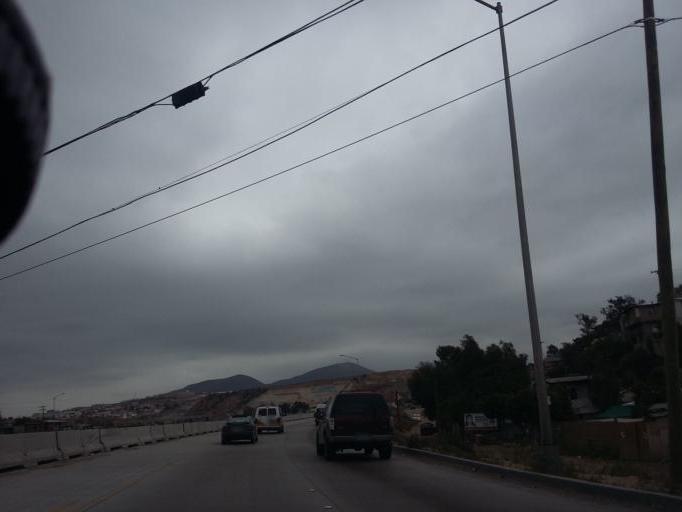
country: MX
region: Baja California
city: Tijuana
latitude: 32.5133
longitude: -116.9522
